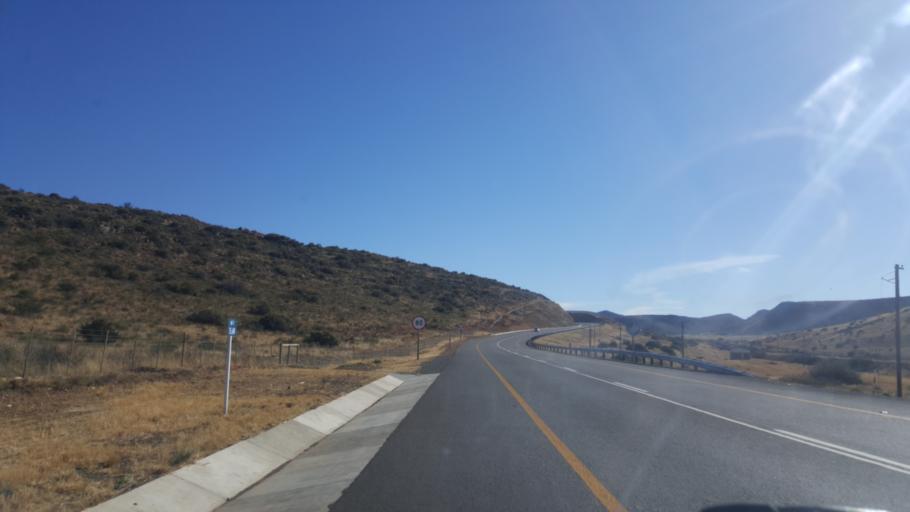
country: ZA
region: Eastern Cape
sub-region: Chris Hani District Municipality
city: Middelburg
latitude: -31.3842
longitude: 25.0320
